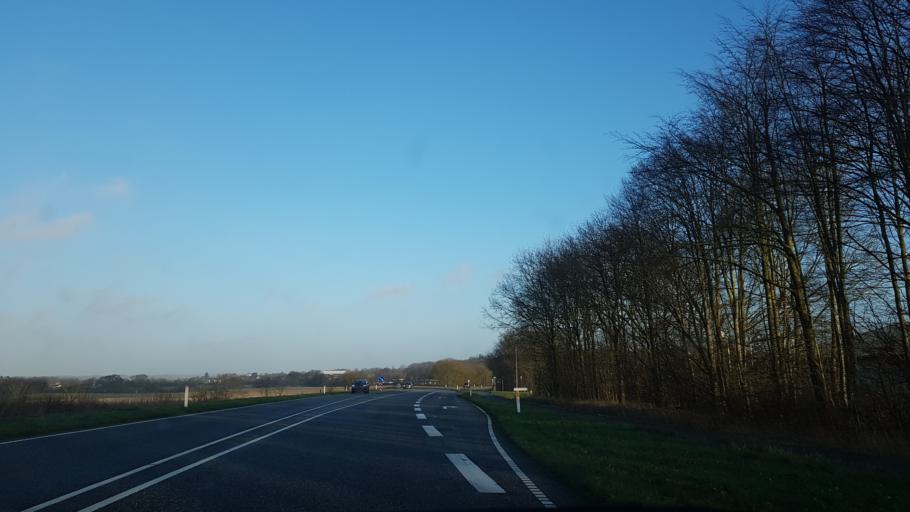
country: DK
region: South Denmark
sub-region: Haderslev Kommune
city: Haderslev
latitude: 55.2239
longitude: 9.4765
